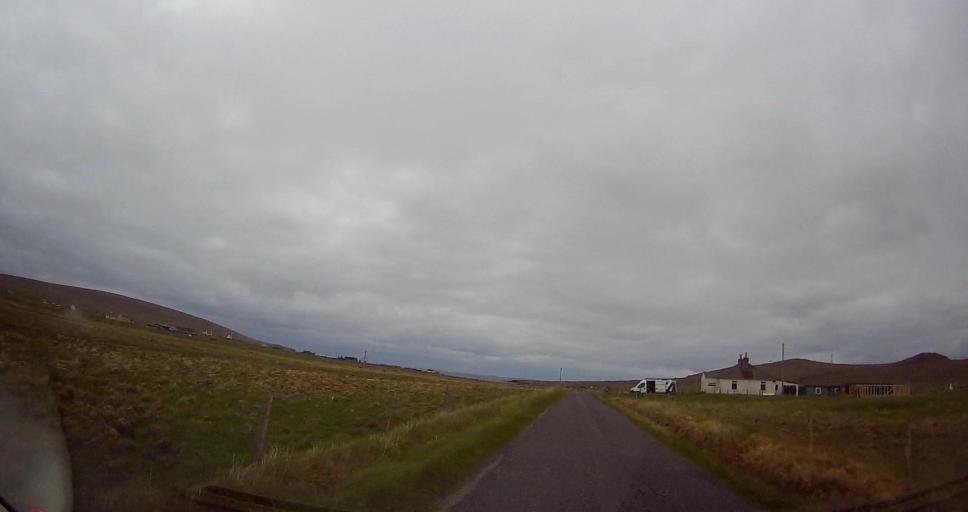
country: GB
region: Scotland
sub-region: Shetland Islands
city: Shetland
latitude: 60.7921
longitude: -0.8480
